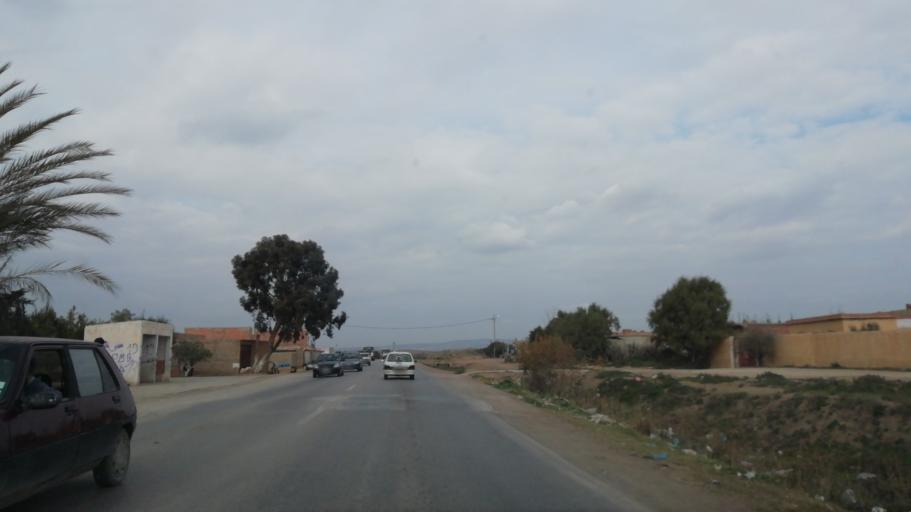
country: DZ
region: Mostaganem
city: Mostaganem
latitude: 35.6988
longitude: 0.0553
